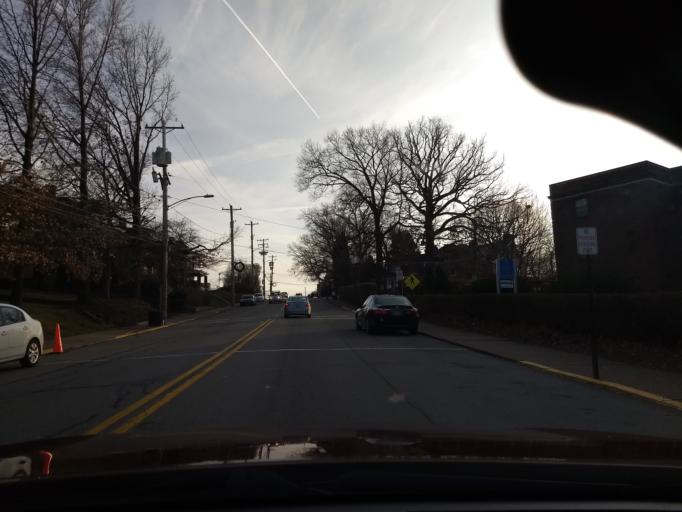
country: US
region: Pennsylvania
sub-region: Allegheny County
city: Brentwood
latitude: 40.3769
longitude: -79.9755
